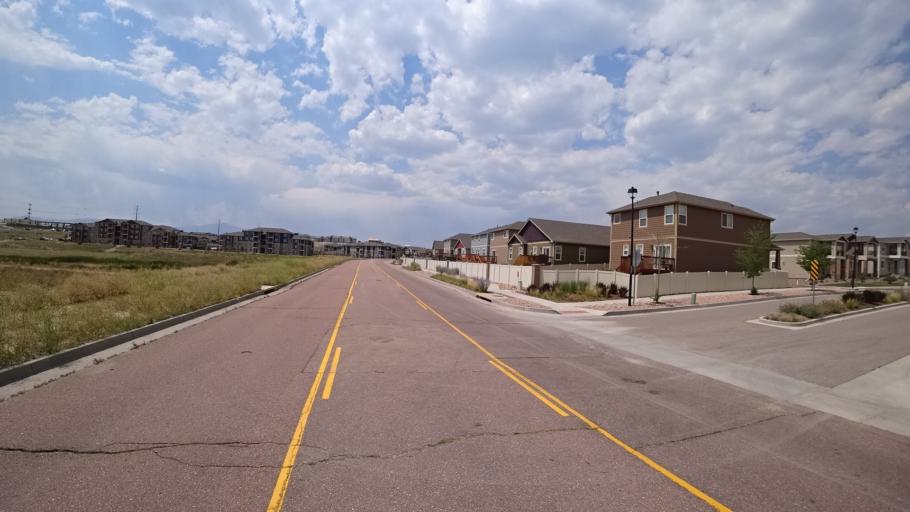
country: US
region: Colorado
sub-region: El Paso County
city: Black Forest
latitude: 38.9437
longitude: -104.6956
